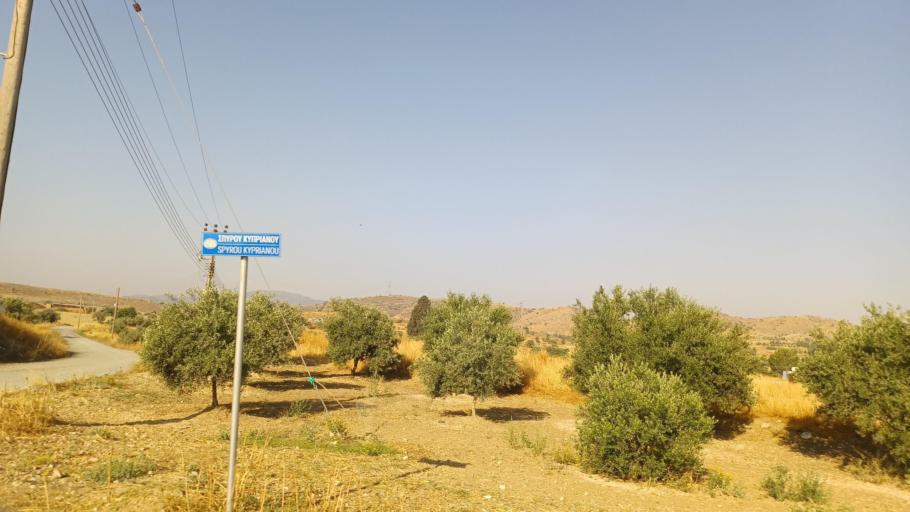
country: CY
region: Lefkosia
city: Lympia
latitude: 34.9928
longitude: 33.4444
